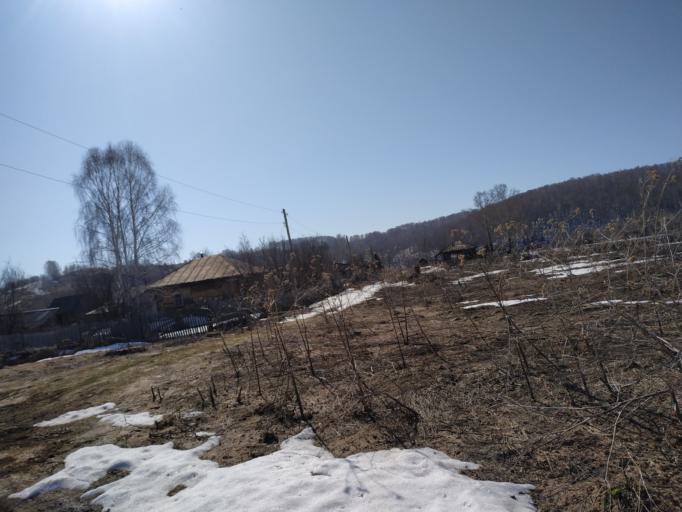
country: RU
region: Altai Krai
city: Krasnogorskoye
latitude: 52.4894
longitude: 86.2413
